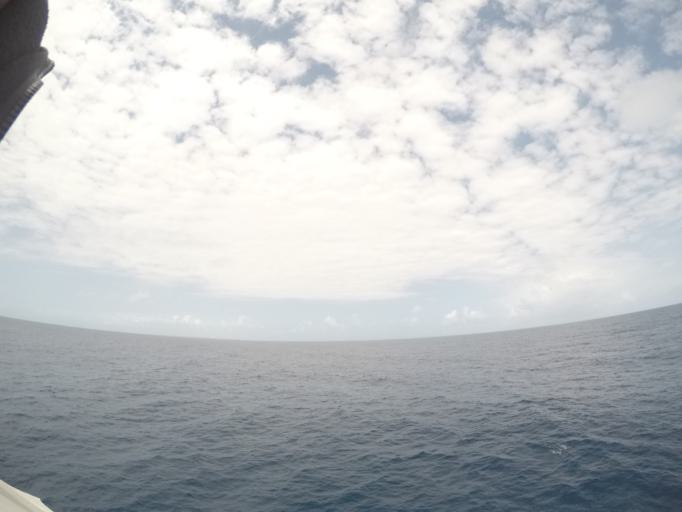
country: TZ
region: Zanzibar North
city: Nungwi
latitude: -5.6061
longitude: 39.3370
